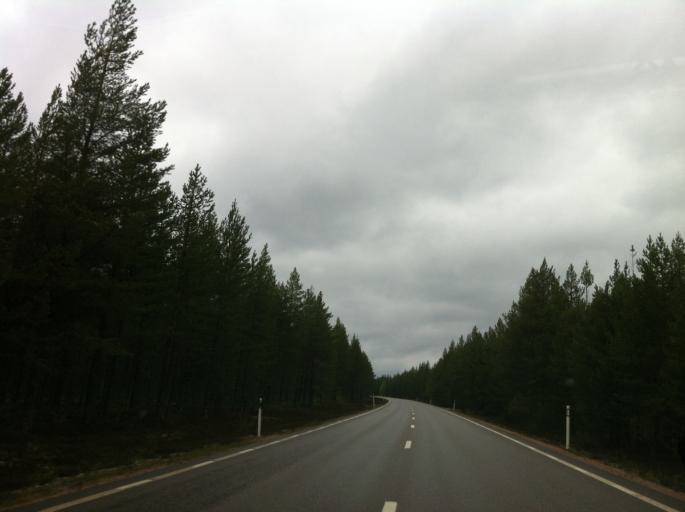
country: SE
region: Jaemtland
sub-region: Harjedalens Kommun
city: Sveg
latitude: 62.0571
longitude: 14.2980
